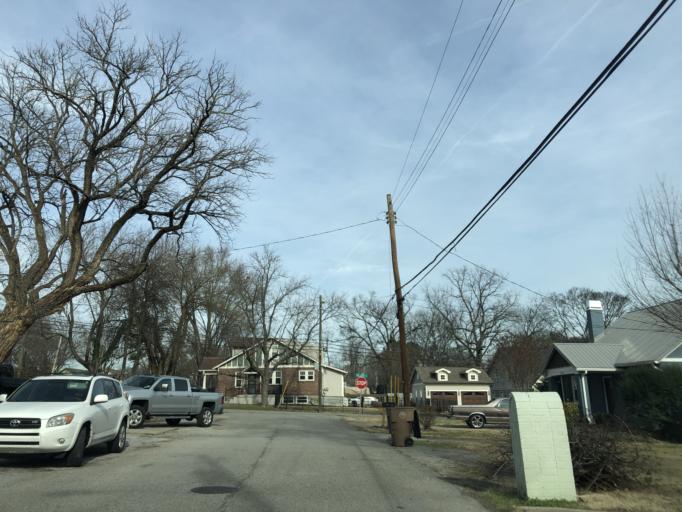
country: US
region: Tennessee
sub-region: Davidson County
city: Nashville
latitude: 36.2147
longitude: -86.7340
